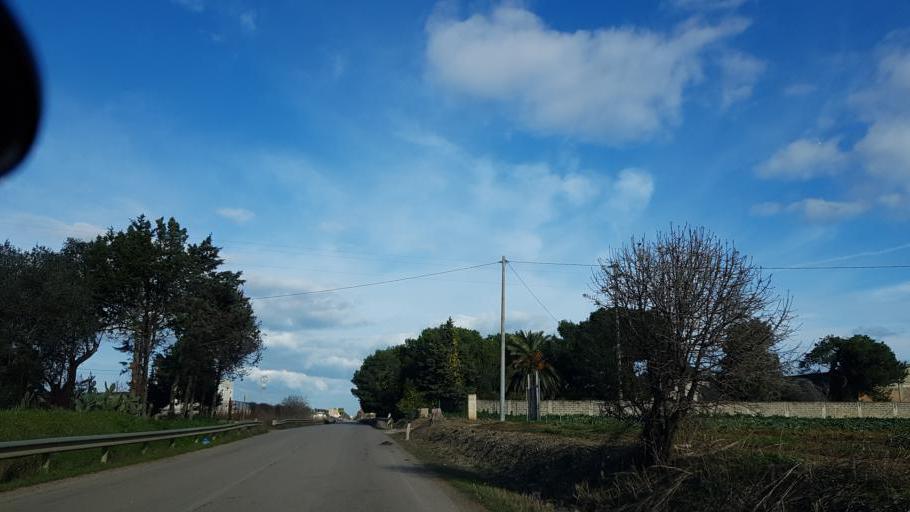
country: IT
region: Apulia
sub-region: Provincia di Brindisi
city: La Rosa
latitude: 40.5966
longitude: 17.9586
